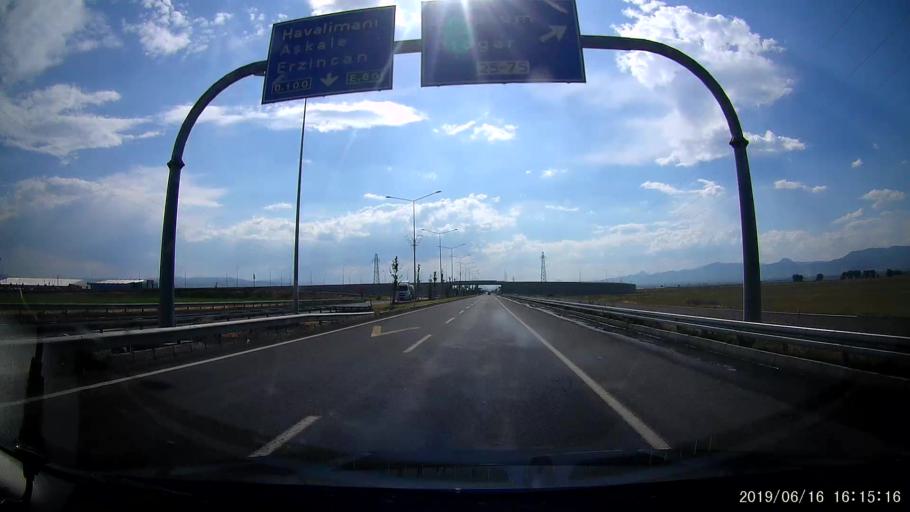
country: TR
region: Erzurum
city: Erzurum
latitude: 39.9617
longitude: 41.2298
